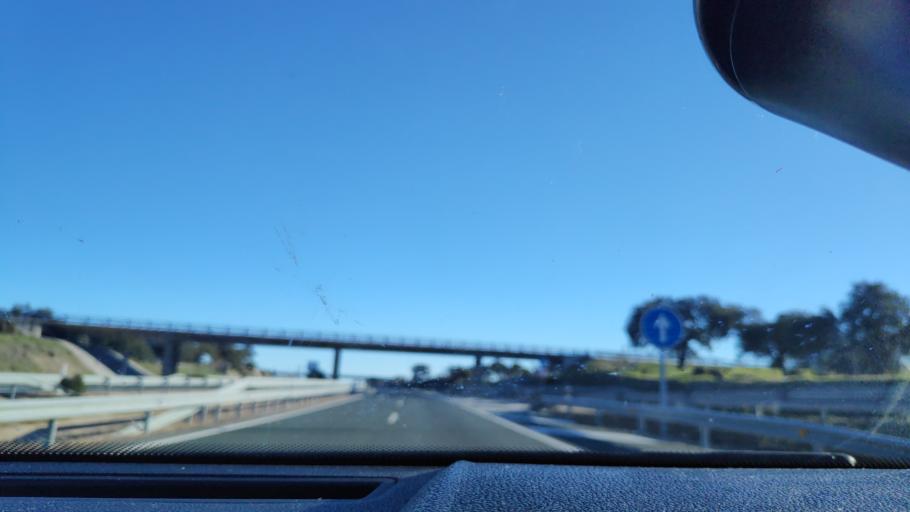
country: ES
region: Andalusia
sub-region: Provincia de Huelva
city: Santa Olalla del Cala
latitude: 37.9188
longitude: -6.2241
